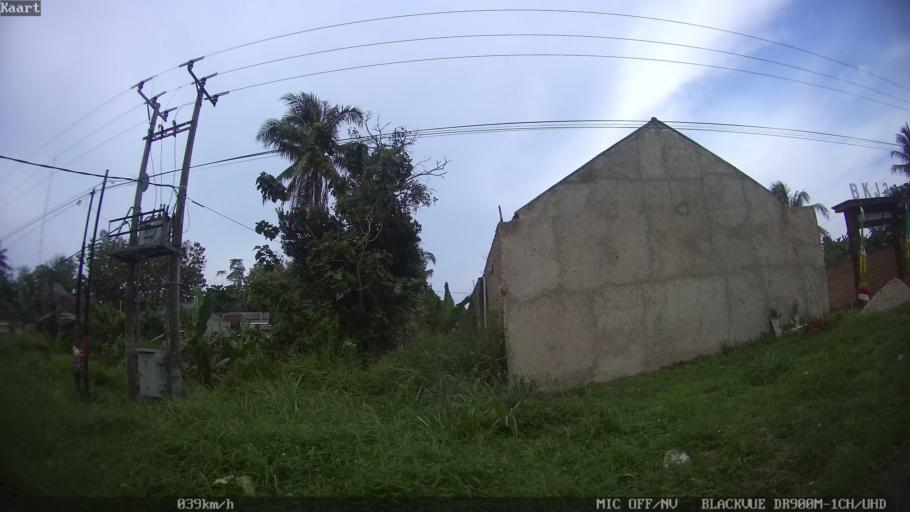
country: ID
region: Lampung
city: Bandarlampung
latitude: -5.4023
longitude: 105.1916
